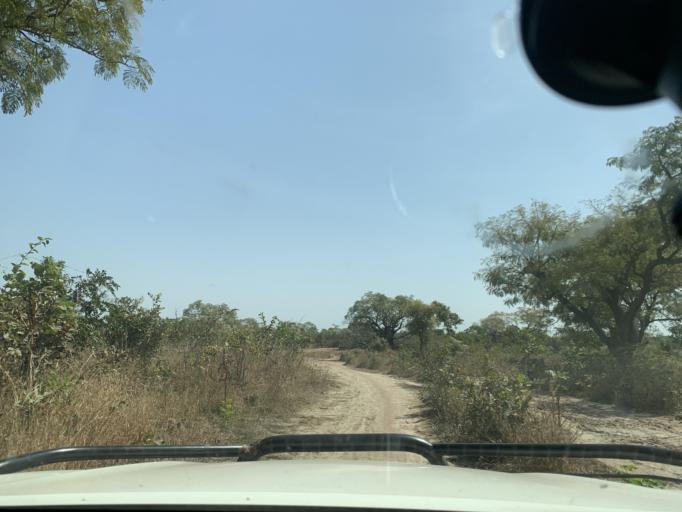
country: ML
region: Sikasso
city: Kolondieba
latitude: 10.8369
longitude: -6.7951
